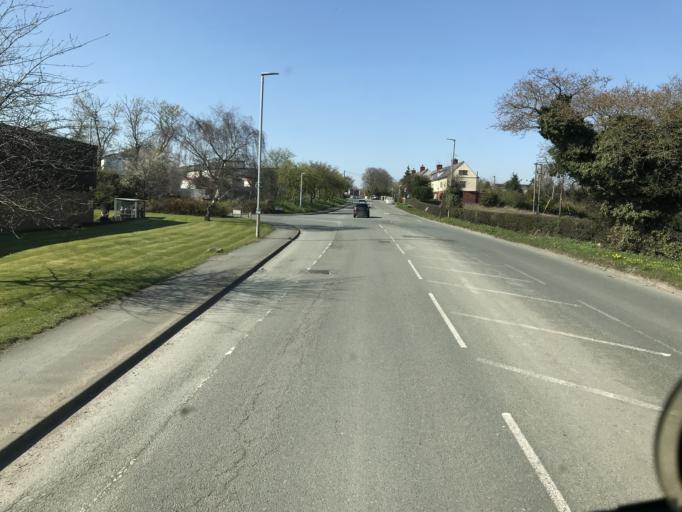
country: GB
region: Wales
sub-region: Wrexham
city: Gresford
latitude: 53.1010
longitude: -3.0007
